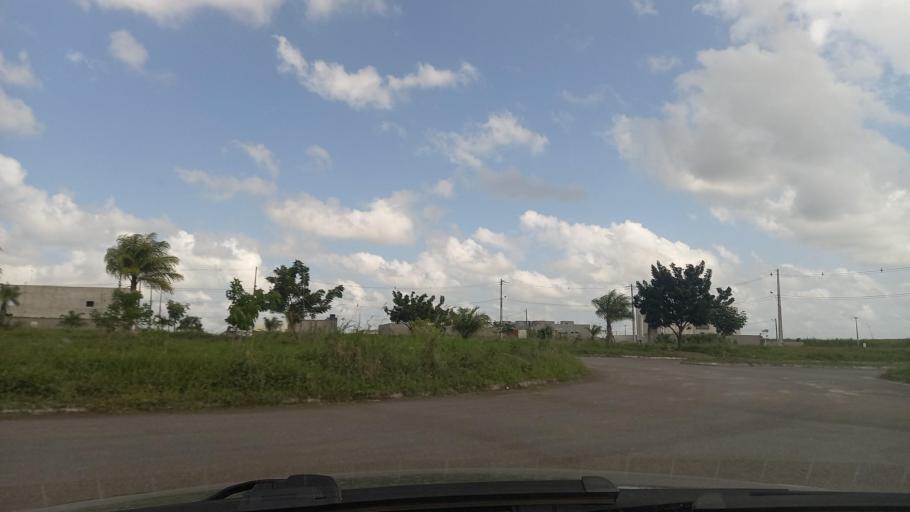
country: BR
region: Pernambuco
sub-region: Goiana
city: Goiana
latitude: -7.5672
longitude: -35.0318
